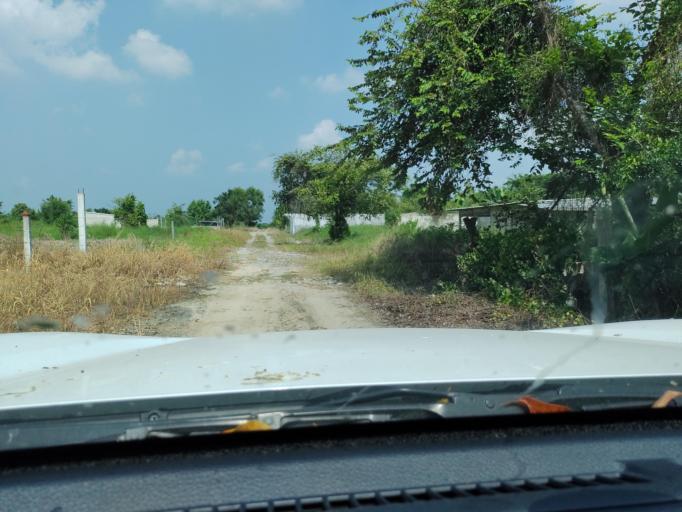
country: MX
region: Veracruz
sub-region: Martinez de la Torre
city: El Progreso
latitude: 20.0689
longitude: -97.0081
